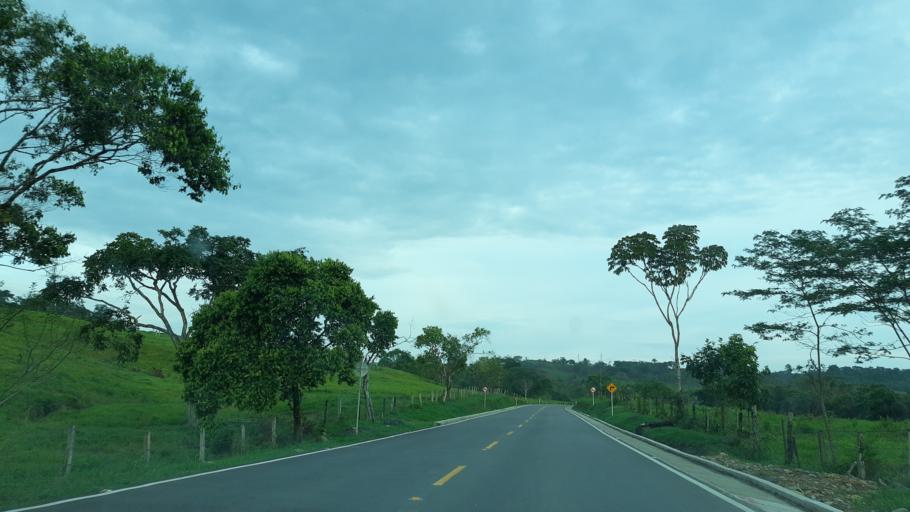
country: CO
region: Casanare
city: Sabanalarga
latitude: 4.8172
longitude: -73.0661
